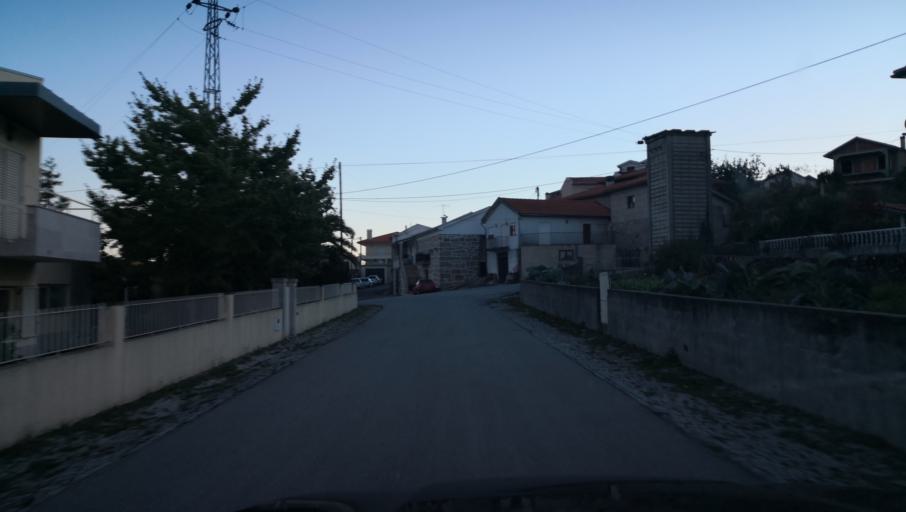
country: PT
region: Vila Real
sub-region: Santa Marta de Penaguiao
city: Santa Marta de Penaguiao
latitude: 41.2624
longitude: -7.7897
